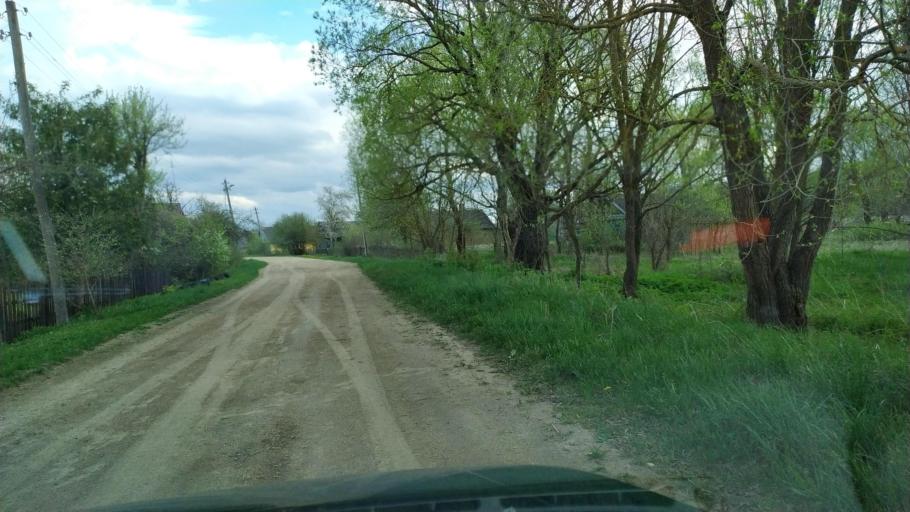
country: BY
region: Brest
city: Pruzhany
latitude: 52.7082
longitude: 24.2590
